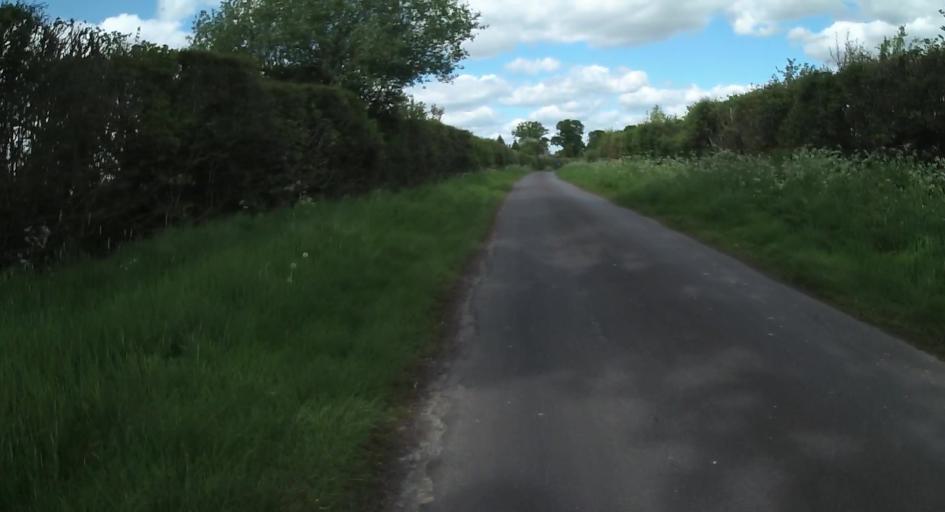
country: GB
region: England
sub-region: West Berkshire
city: Stratfield Mortimer
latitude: 51.3385
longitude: -1.0431
